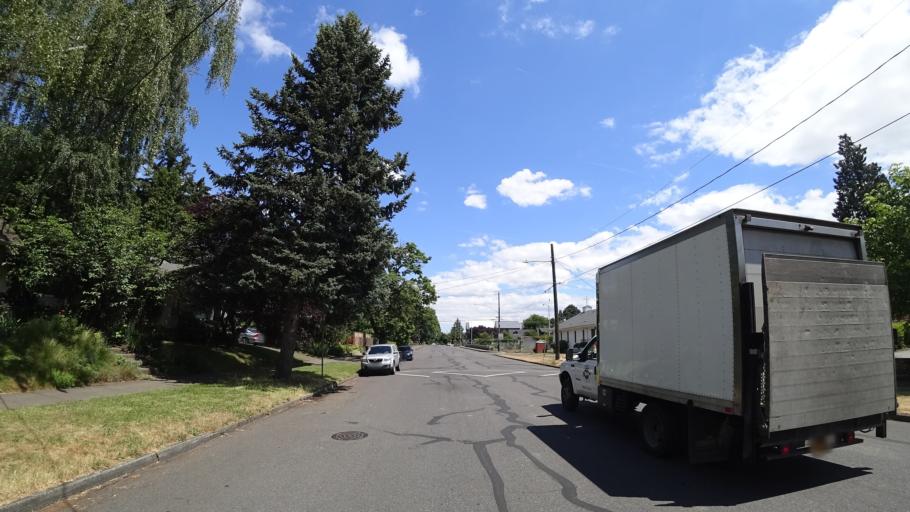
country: US
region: Oregon
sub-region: Multnomah County
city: Portland
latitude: 45.5664
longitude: -122.6800
